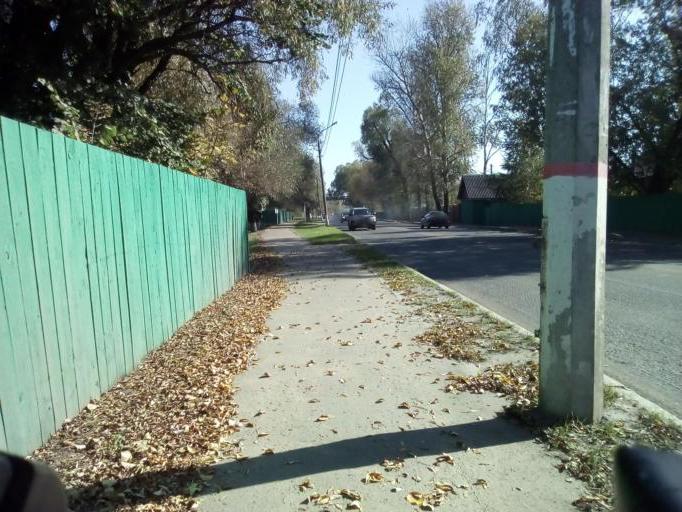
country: RU
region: Moskovskaya
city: Ramenskoye
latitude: 55.5561
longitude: 38.2636
